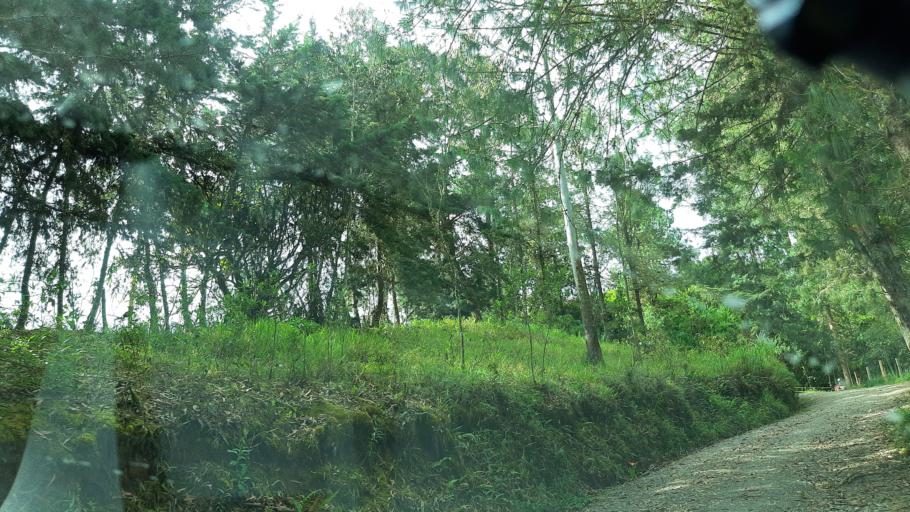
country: CO
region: Boyaca
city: Garagoa
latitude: 5.0373
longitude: -73.3472
